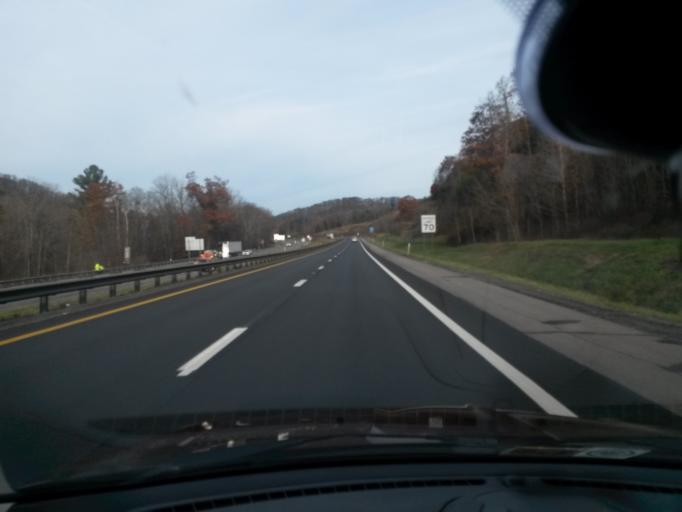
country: US
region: West Virginia
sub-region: Raleigh County
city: Prosperity
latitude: 37.8398
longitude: -81.2268
